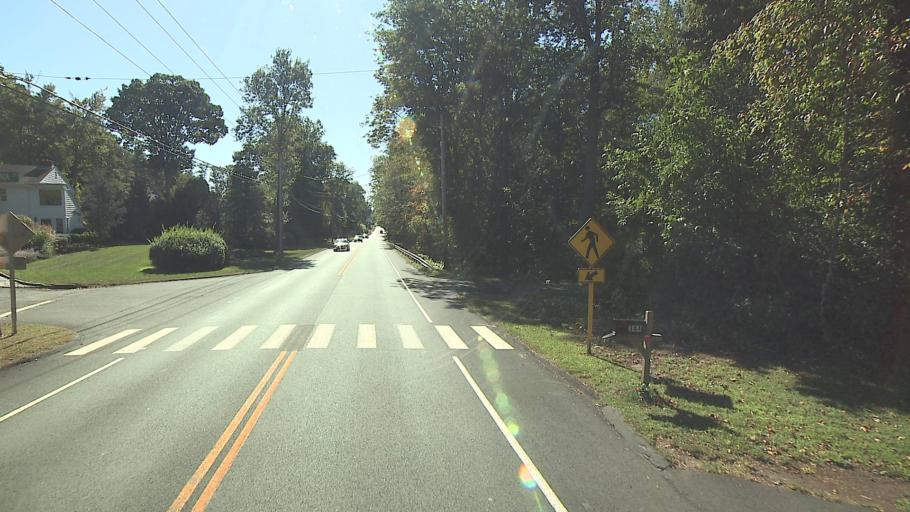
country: US
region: Connecticut
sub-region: New Haven County
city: Orange
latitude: 41.2733
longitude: -73.0041
